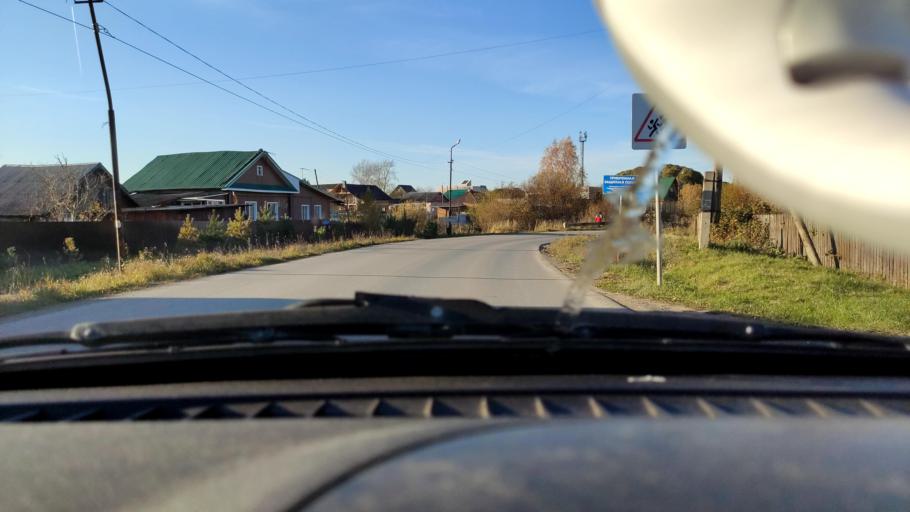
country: RU
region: Perm
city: Froly
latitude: 57.8846
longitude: 56.2581
